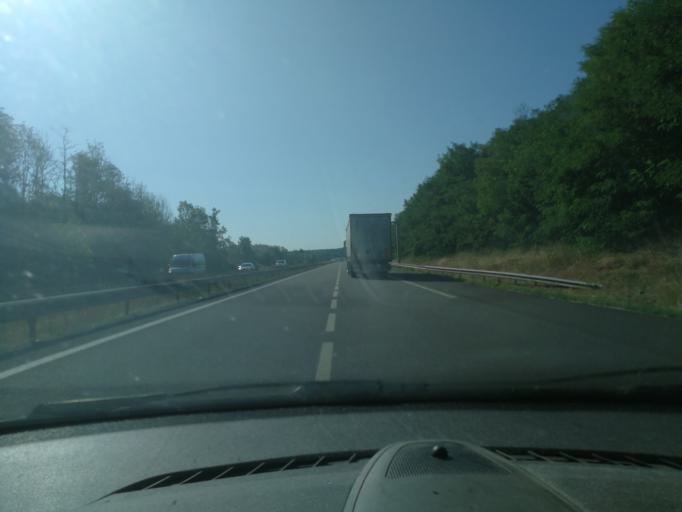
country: FR
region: Lorraine
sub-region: Departement de la Moselle
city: Seingbouse
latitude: 49.1118
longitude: 6.8494
